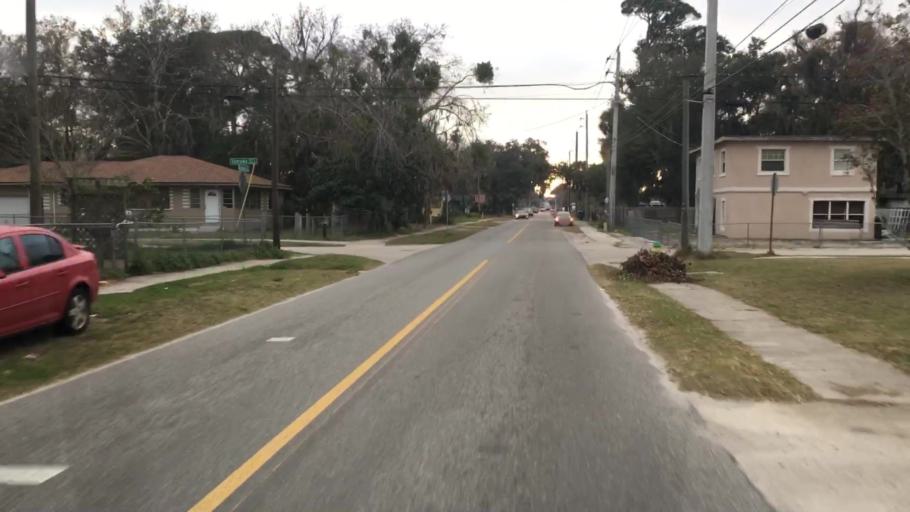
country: US
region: Florida
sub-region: Volusia County
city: Daytona Beach
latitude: 29.2184
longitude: -81.0422
